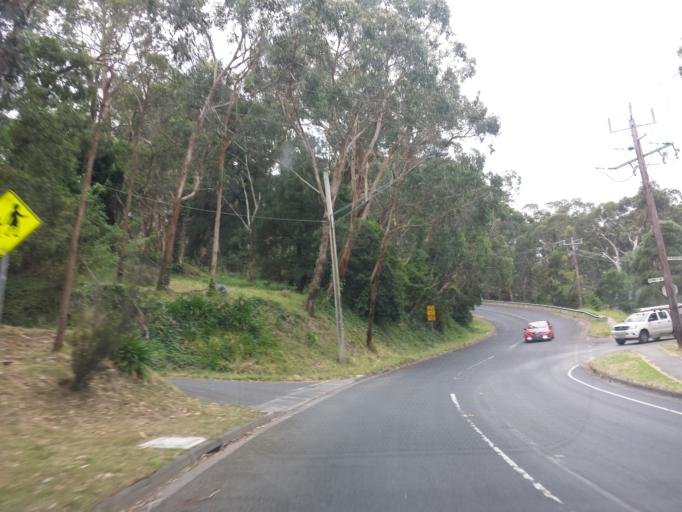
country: AU
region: Victoria
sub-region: Yarra Ranges
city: Tremont
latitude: -37.9154
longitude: 145.3251
